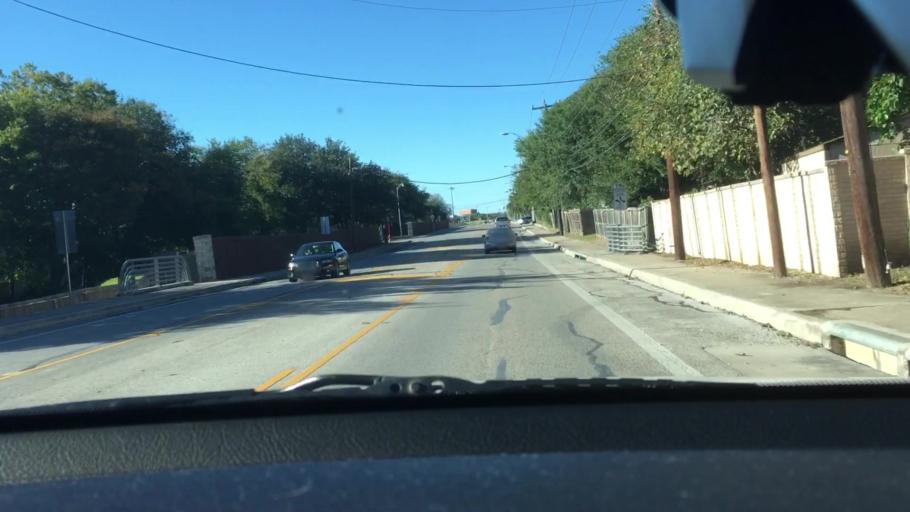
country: US
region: Texas
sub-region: Bexar County
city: Converse
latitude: 29.5371
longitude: -98.3155
